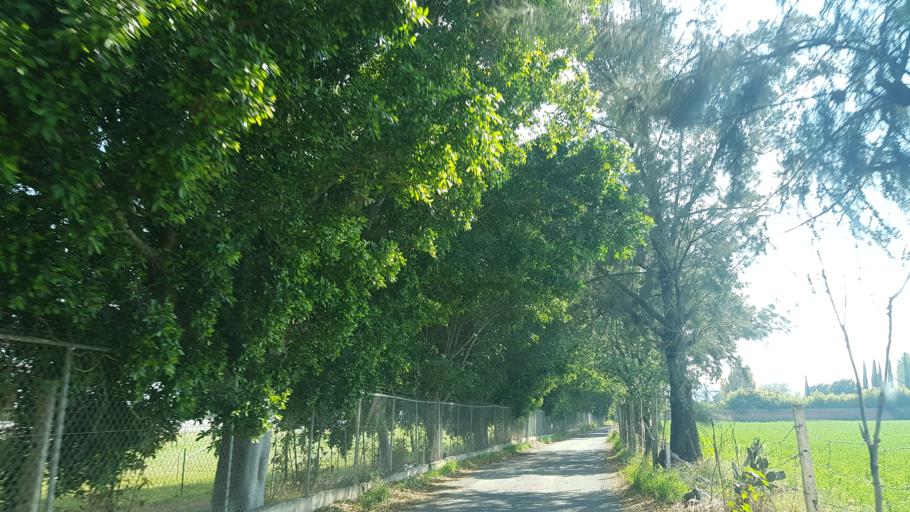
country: MX
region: Puebla
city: Atlixco
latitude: 18.8776
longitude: -98.4850
